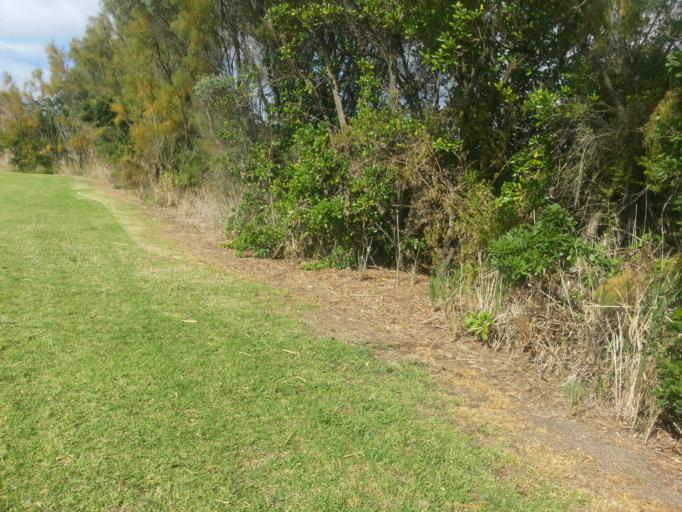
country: AU
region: Victoria
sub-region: Warrnambool
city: Warrnambool
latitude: -38.3913
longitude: 142.4767
